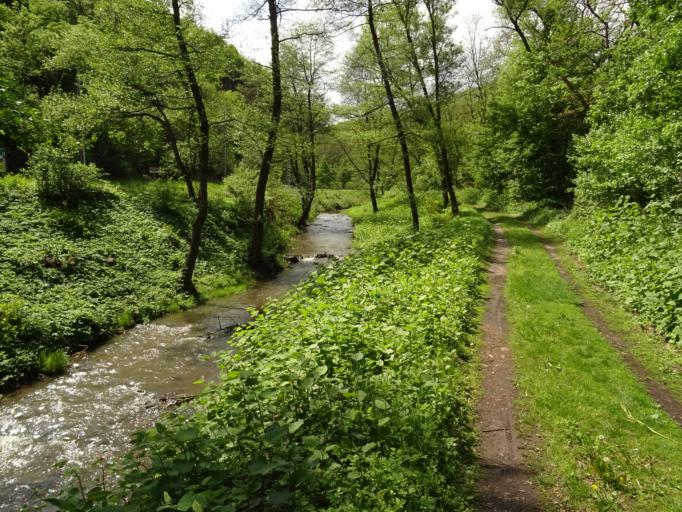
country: HU
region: Heves
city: Belapatfalva
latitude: 47.9871
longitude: 20.3367
